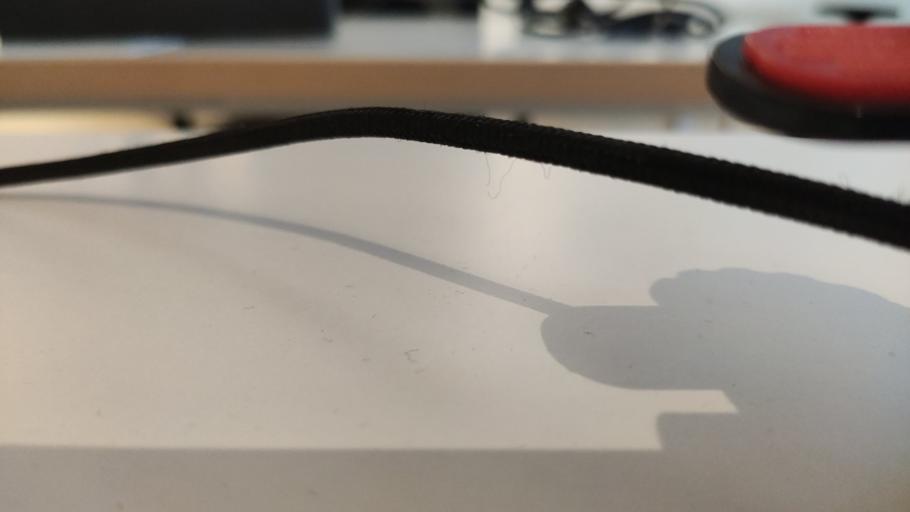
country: RU
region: Moskovskaya
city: Novopetrovskoye
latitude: 55.8606
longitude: 36.3838
